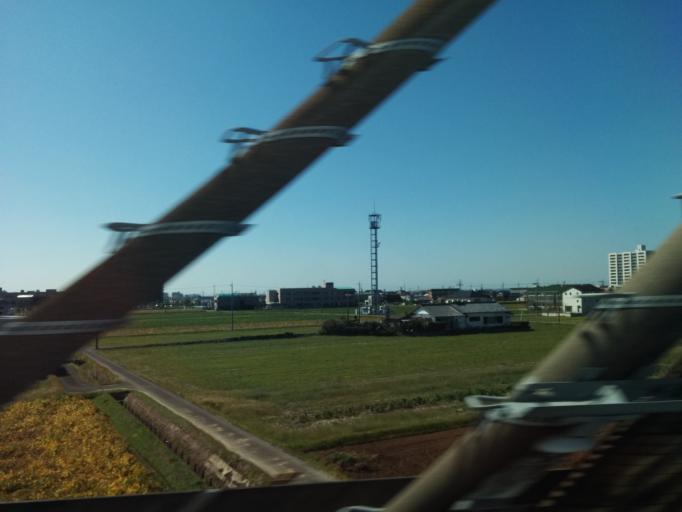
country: JP
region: Aichi
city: Anjo
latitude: 34.9455
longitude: 137.0822
